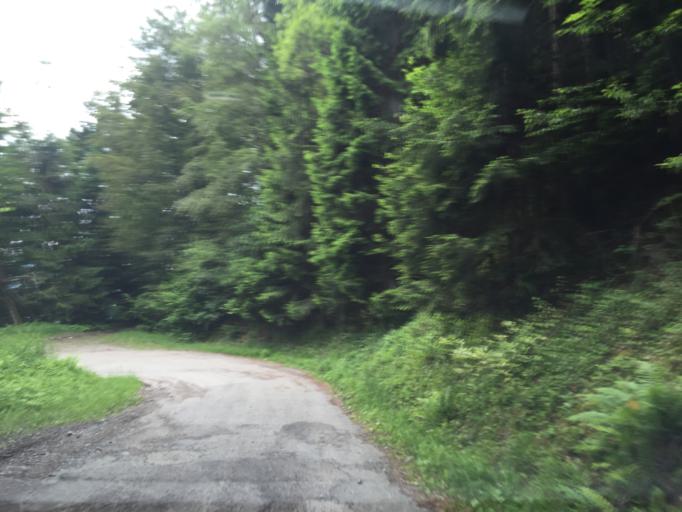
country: FR
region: Rhone-Alpes
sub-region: Departement de la Savoie
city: La Rochette
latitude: 45.4347
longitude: 6.1698
